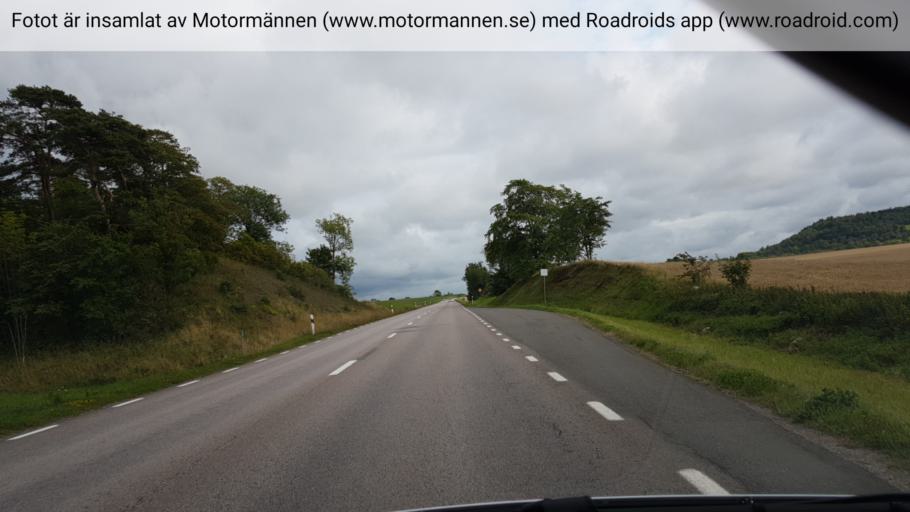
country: SE
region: Vaestra Goetaland
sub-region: Falkopings Kommun
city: Falkoeping
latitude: 58.1554
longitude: 13.5901
